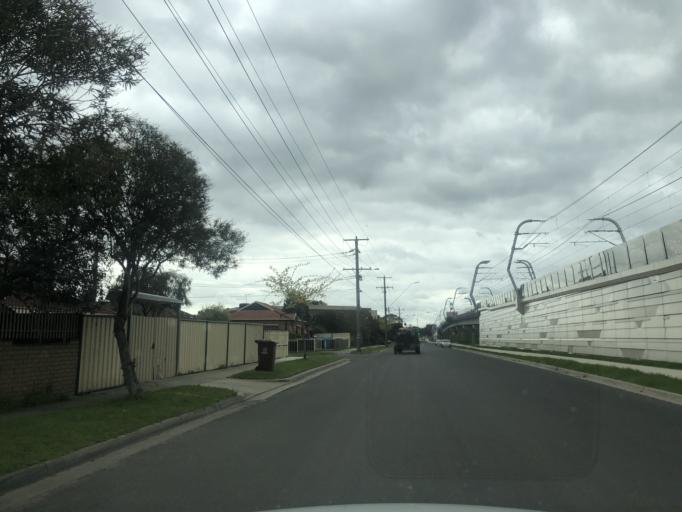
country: AU
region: Victoria
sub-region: Greater Dandenong
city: Dandenong
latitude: -37.9754
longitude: 145.1874
